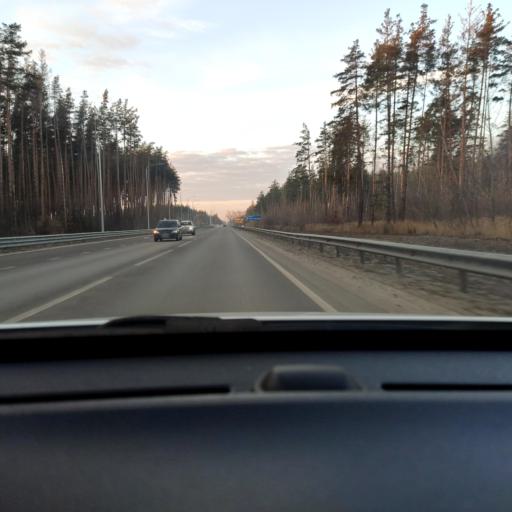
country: RU
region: Voronezj
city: Somovo
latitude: 51.6951
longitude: 39.3101
